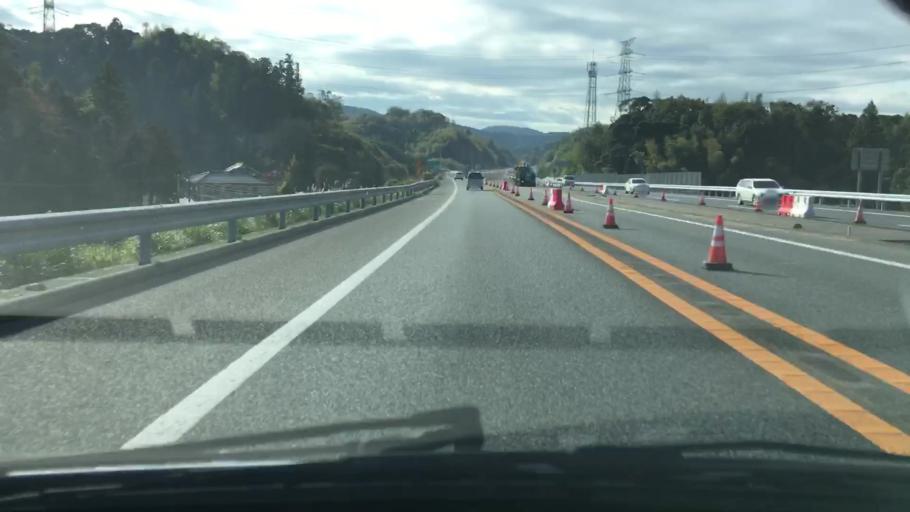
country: JP
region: Chiba
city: Kimitsu
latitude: 35.2877
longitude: 139.9286
